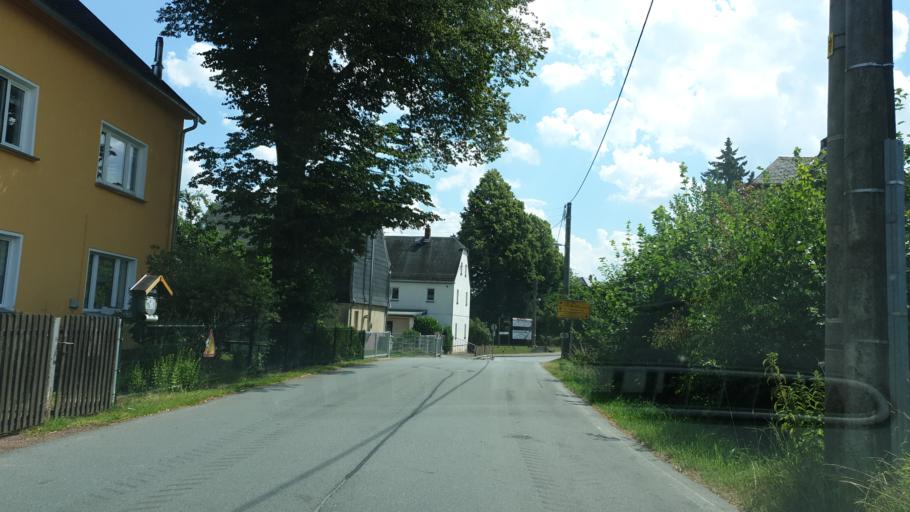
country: DE
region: Saxony
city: Kirchberg
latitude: 50.7949
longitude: 12.7851
